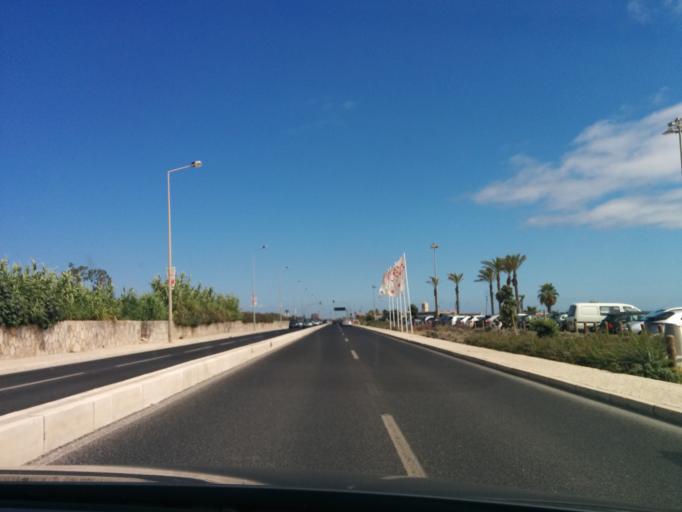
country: PT
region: Lisbon
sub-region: Oeiras
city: Carcavelos
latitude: 38.6803
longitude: -9.3346
